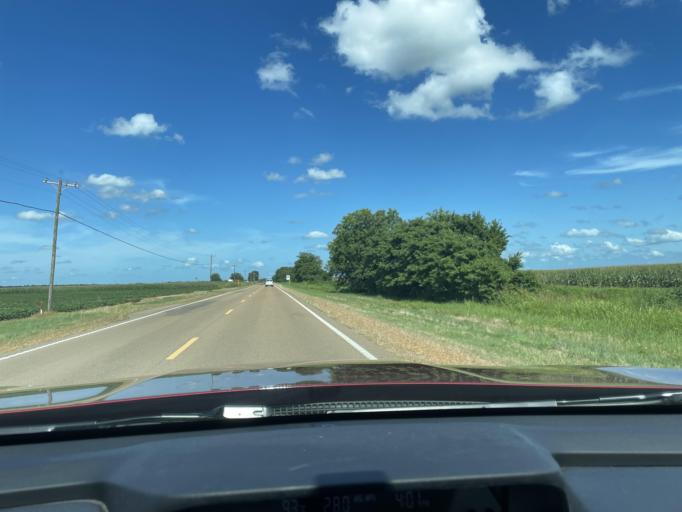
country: US
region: Mississippi
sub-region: Humphreys County
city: Belzoni
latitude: 33.1837
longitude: -90.5335
